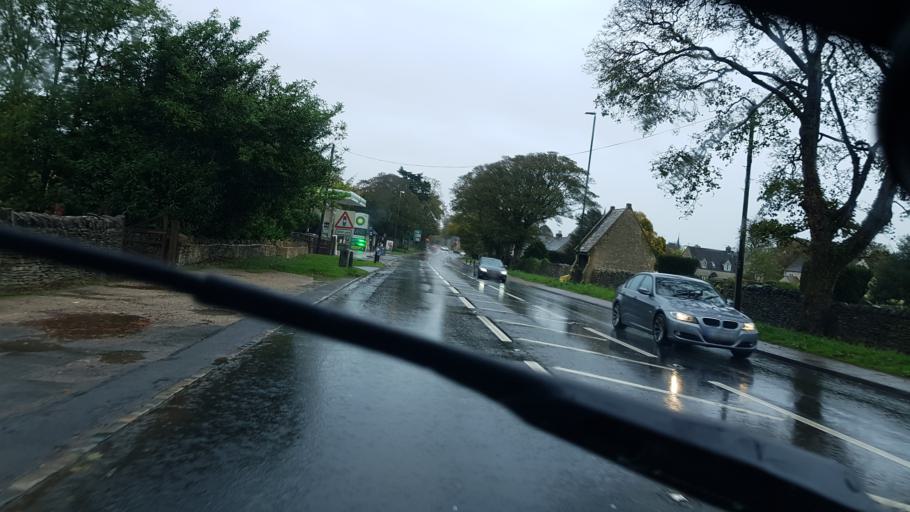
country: GB
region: England
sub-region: Gloucestershire
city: Stow on the Wold
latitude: 51.9272
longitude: -1.7255
